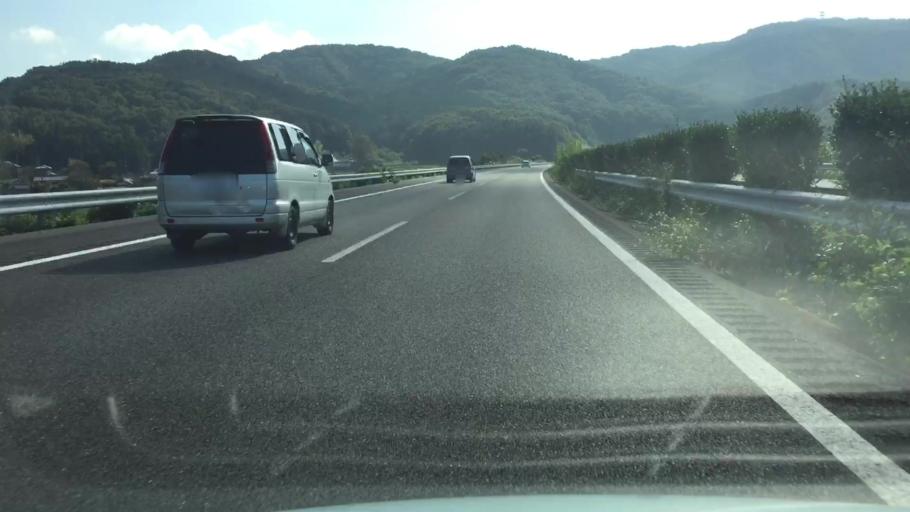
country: JP
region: Ibaraki
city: Iwase
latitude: 36.3523
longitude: 140.1000
